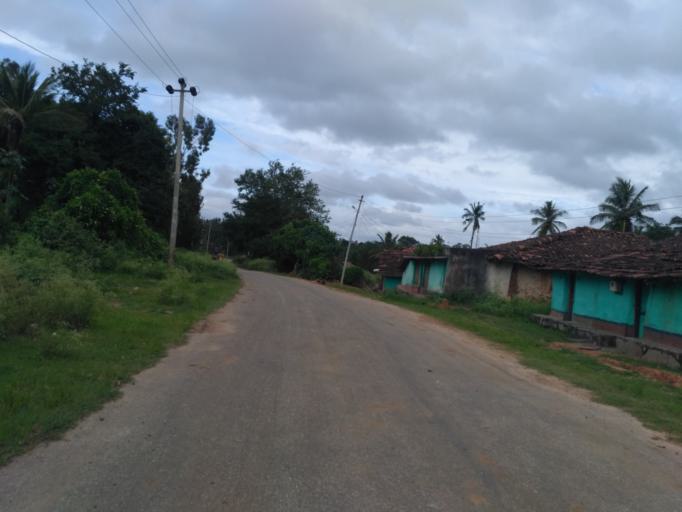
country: IN
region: Karnataka
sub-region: Hassan
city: Gorur
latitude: 12.8234
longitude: 76.0877
